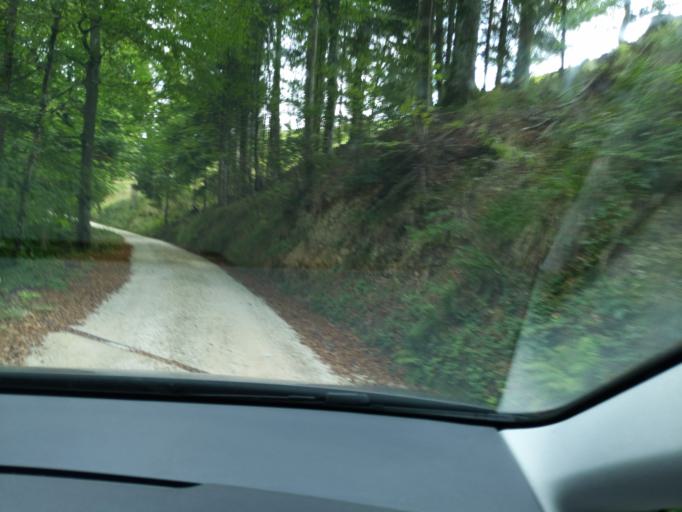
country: CH
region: Bern
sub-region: Oberaargau
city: Wyssachen
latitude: 47.0274
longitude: 7.8323
